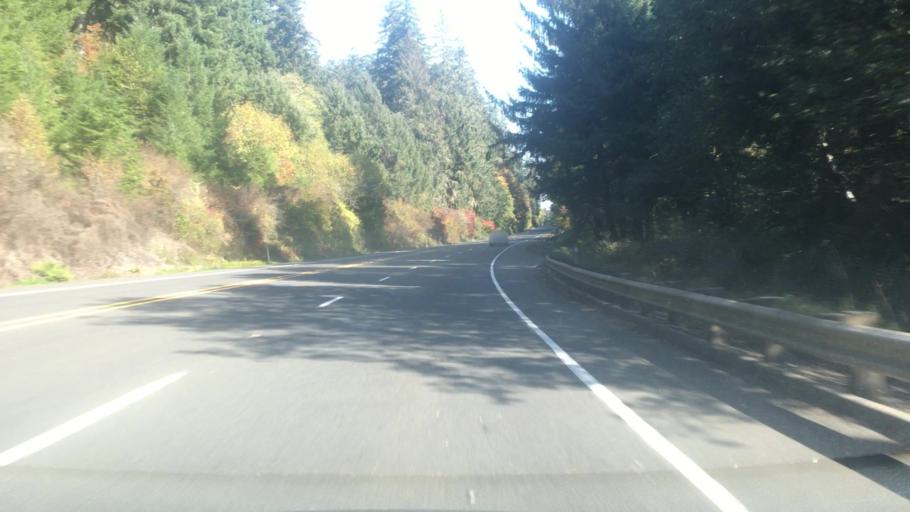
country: US
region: Oregon
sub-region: Lincoln County
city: Rose Lodge
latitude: 45.0472
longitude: -123.7977
